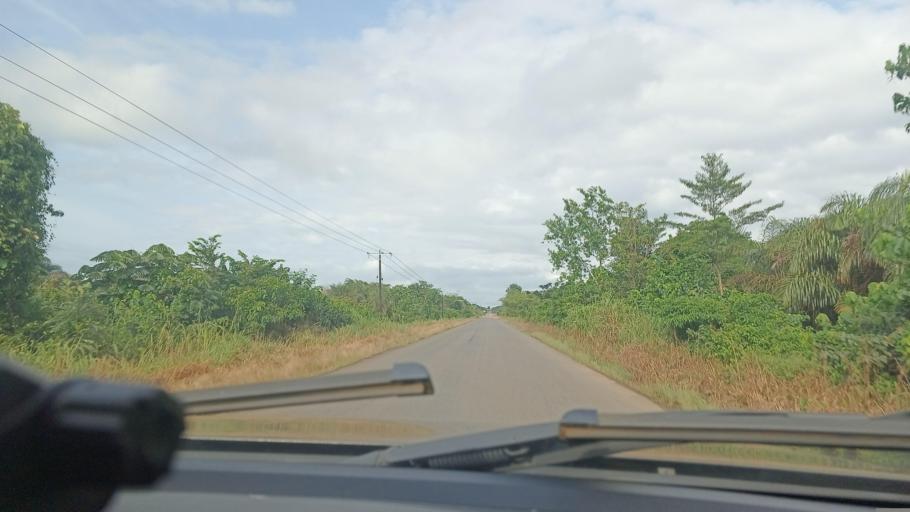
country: LR
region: Bomi
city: Tubmanburg
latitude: 6.7120
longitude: -10.9537
